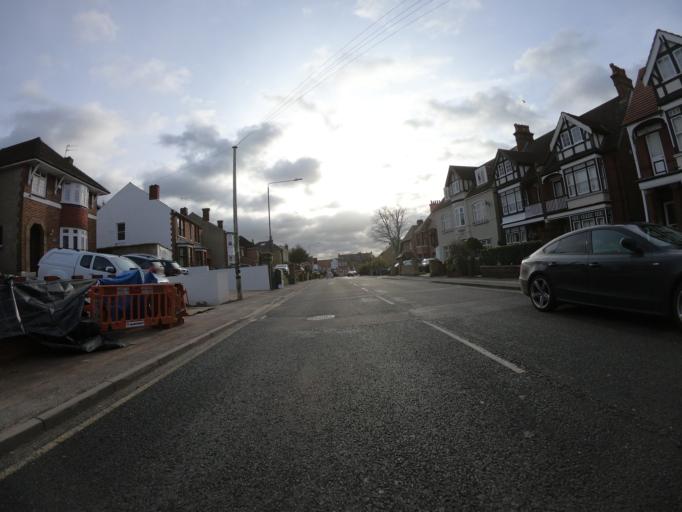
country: GB
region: England
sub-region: Kent
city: Gravesend
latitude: 51.4349
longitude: 0.3665
